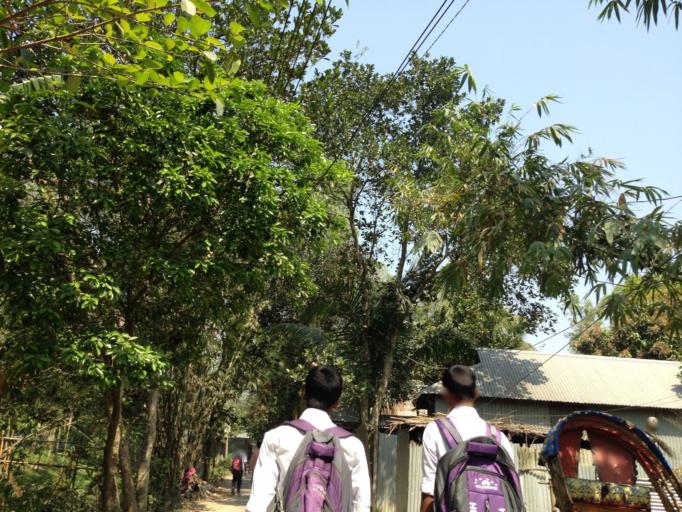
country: BD
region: Dhaka
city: Tangail
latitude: 24.2424
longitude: 89.8900
